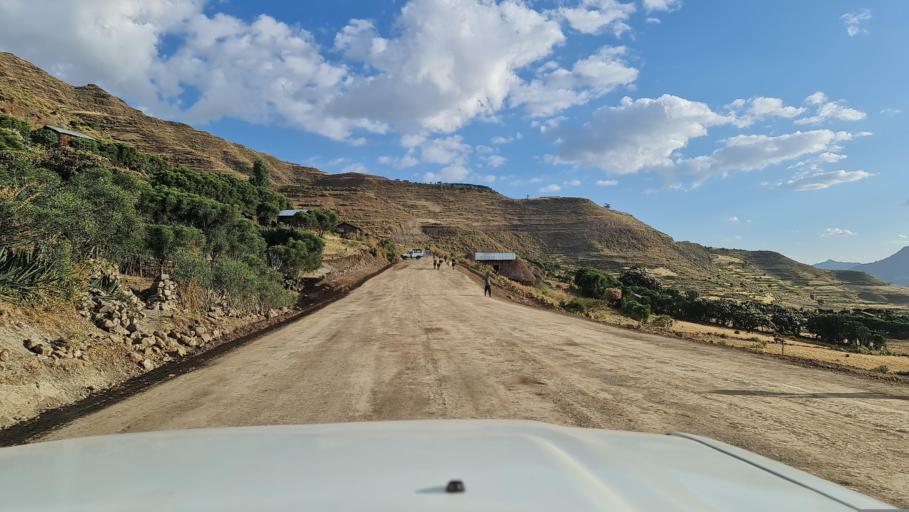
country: ET
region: Amhara
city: Debark'
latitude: 13.0559
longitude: 38.0179
